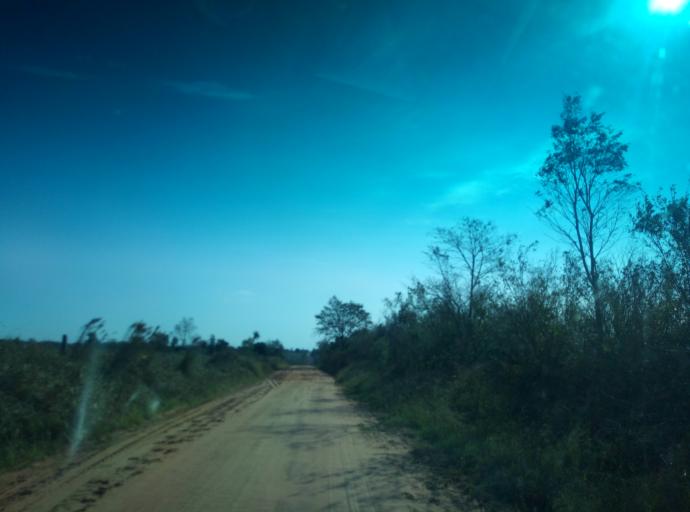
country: PY
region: Caaguazu
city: Doctor Cecilio Baez
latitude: -25.1648
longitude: -56.2189
